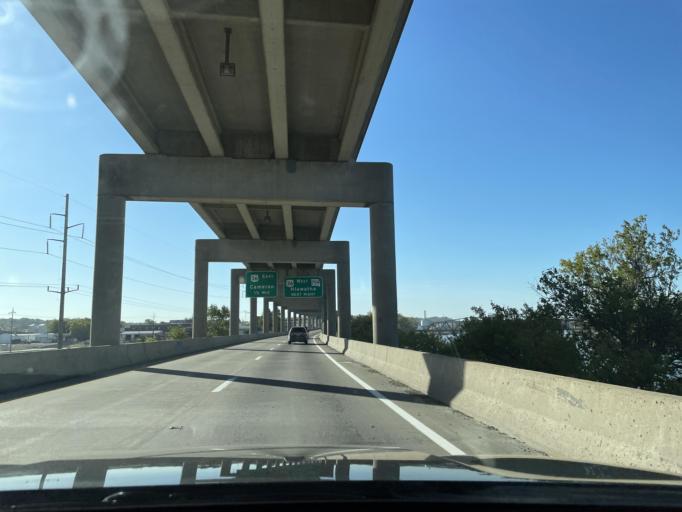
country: US
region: Missouri
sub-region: Buchanan County
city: Saint Joseph
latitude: 39.7597
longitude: -94.8573
